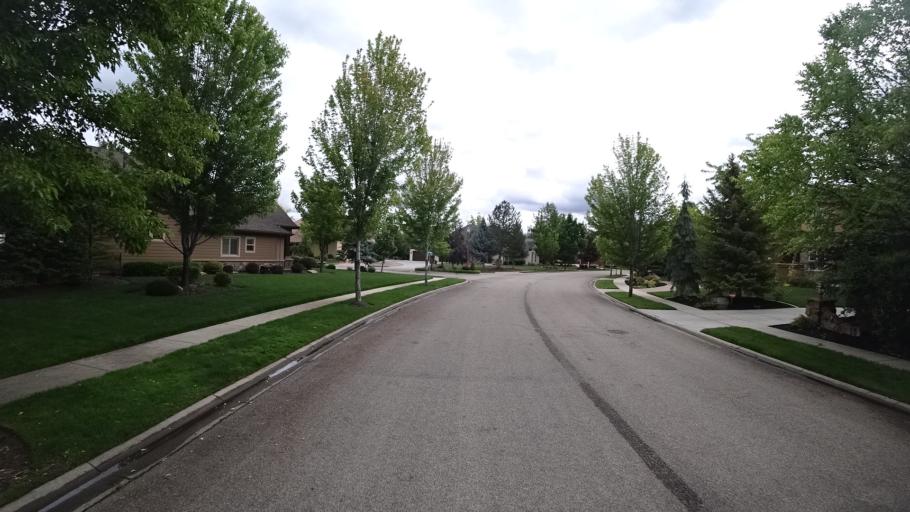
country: US
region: Idaho
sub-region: Ada County
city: Eagle
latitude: 43.6825
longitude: -116.3636
